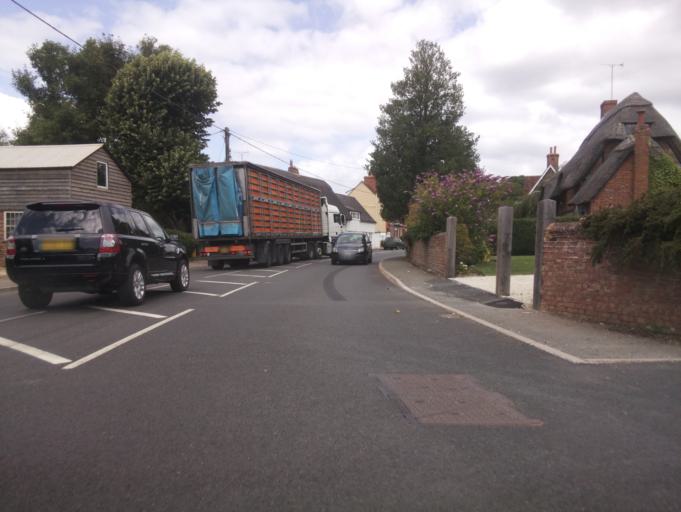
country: GB
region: England
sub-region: Buckinghamshire
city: Newton Longville
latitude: 51.9511
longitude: -0.8129
